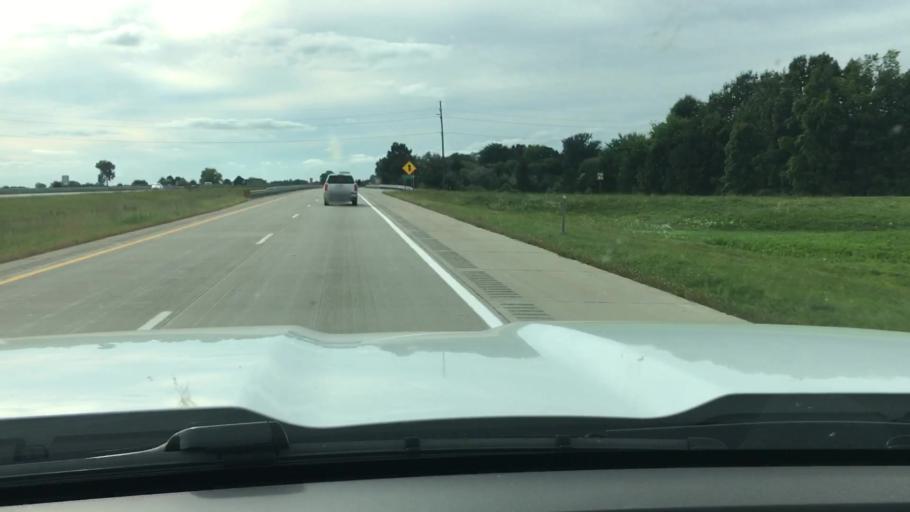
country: US
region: Michigan
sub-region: Lapeer County
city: Lapeer
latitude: 43.0247
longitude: -83.3169
